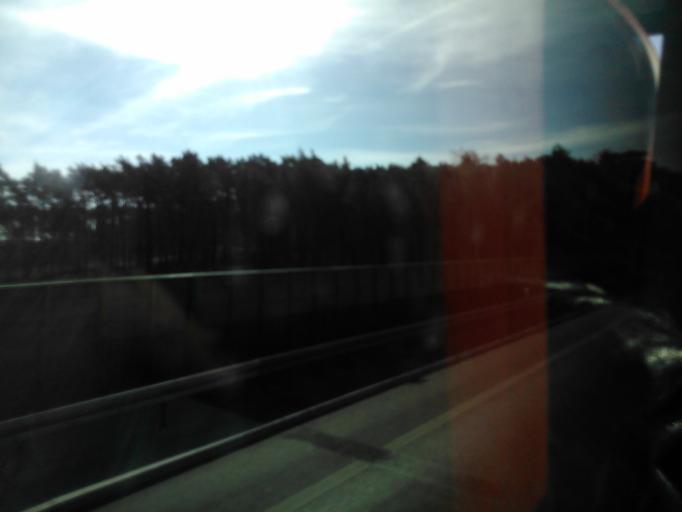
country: PL
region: Kujawsko-Pomorskie
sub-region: Powiat aleksandrowski
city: Aleksandrow Kujawski
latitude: 52.9269
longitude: 18.7085
